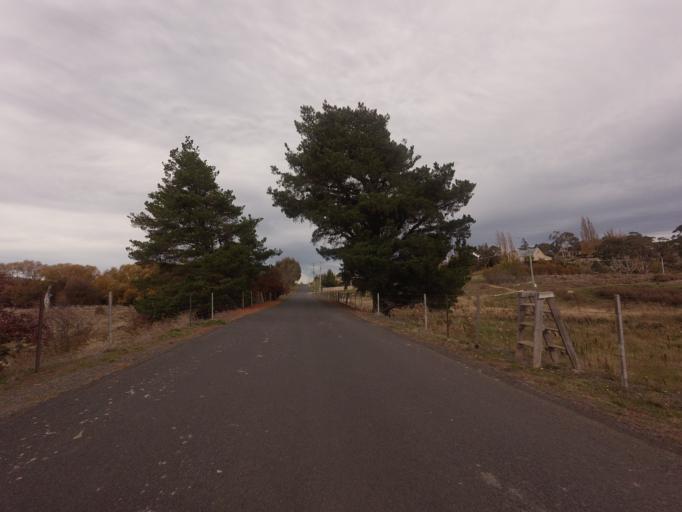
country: AU
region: Tasmania
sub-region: Derwent Valley
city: New Norfolk
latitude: -42.3787
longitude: 147.0004
